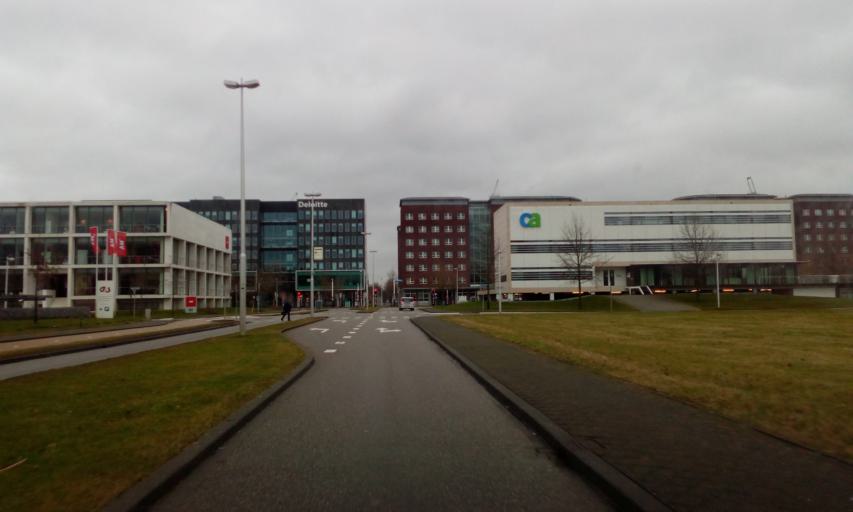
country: NL
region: Utrecht
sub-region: Gemeente Nieuwegein
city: Nieuwegein
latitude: 52.0666
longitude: 5.0803
